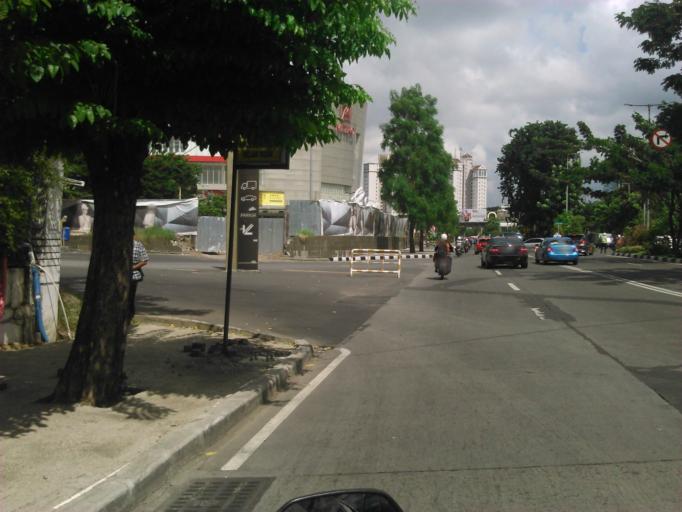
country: ID
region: East Java
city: Jagirsidosermo
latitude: -7.2921
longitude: 112.7210
